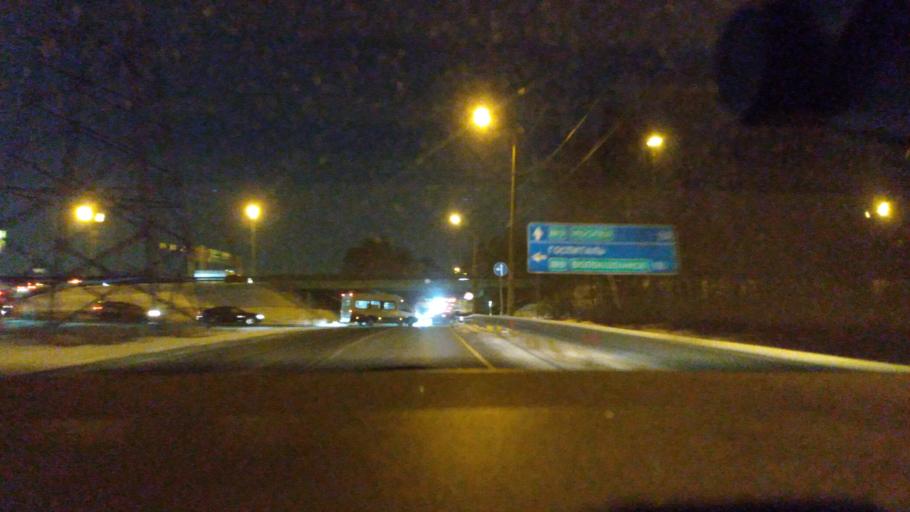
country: RU
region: Moskovskaya
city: Arkhangel'skoye
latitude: 55.8033
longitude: 37.2891
